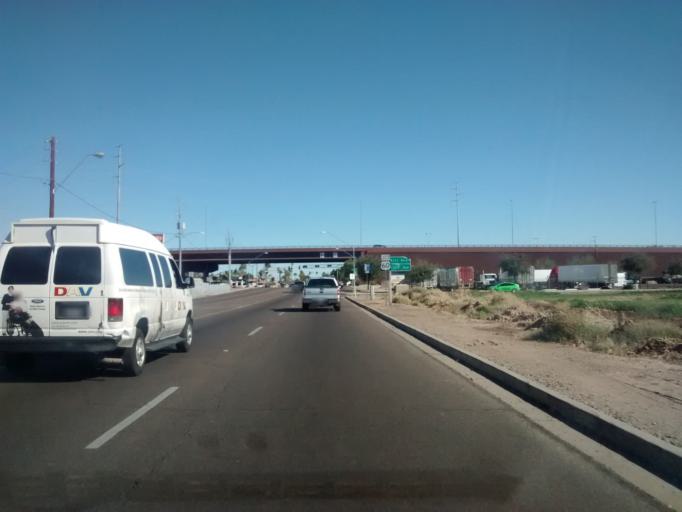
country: US
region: Arizona
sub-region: Maricopa County
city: Glendale
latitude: 33.5239
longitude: -112.1714
